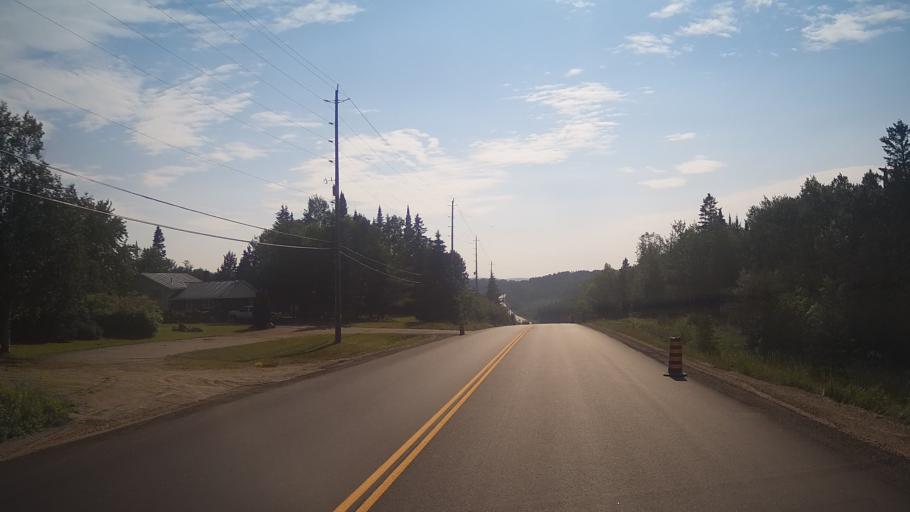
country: CA
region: Ontario
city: Bancroft
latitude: 45.4906
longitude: -78.2116
